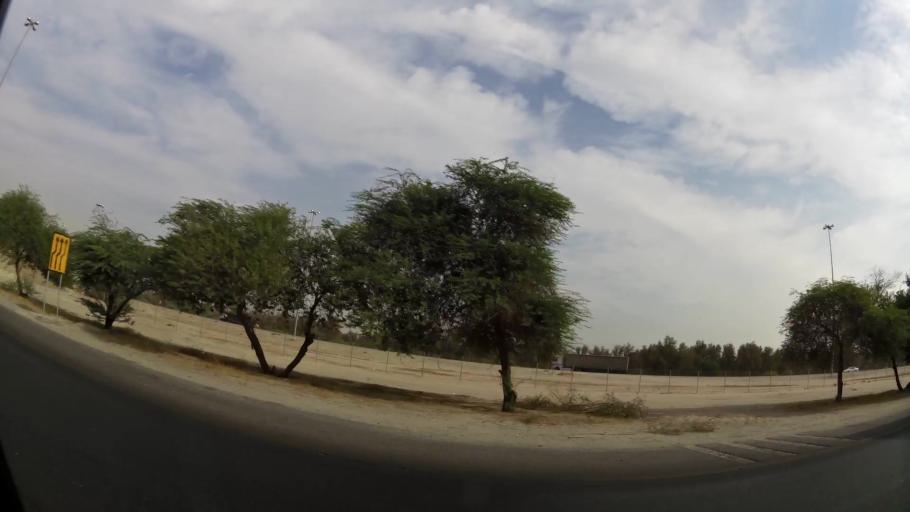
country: KW
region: Al Asimah
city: Ar Rabiyah
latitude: 29.2815
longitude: 47.7917
